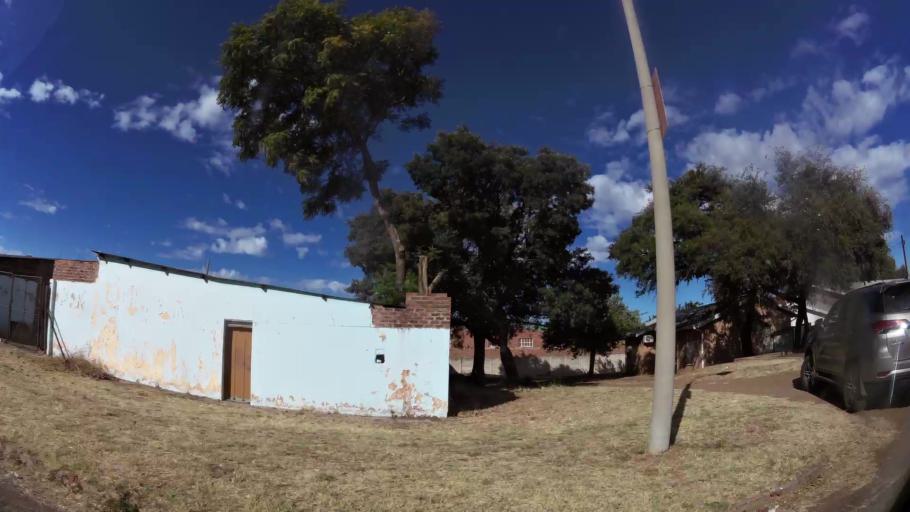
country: ZA
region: Limpopo
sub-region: Waterberg District Municipality
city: Warmbaths
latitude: -24.8805
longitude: 28.2764
